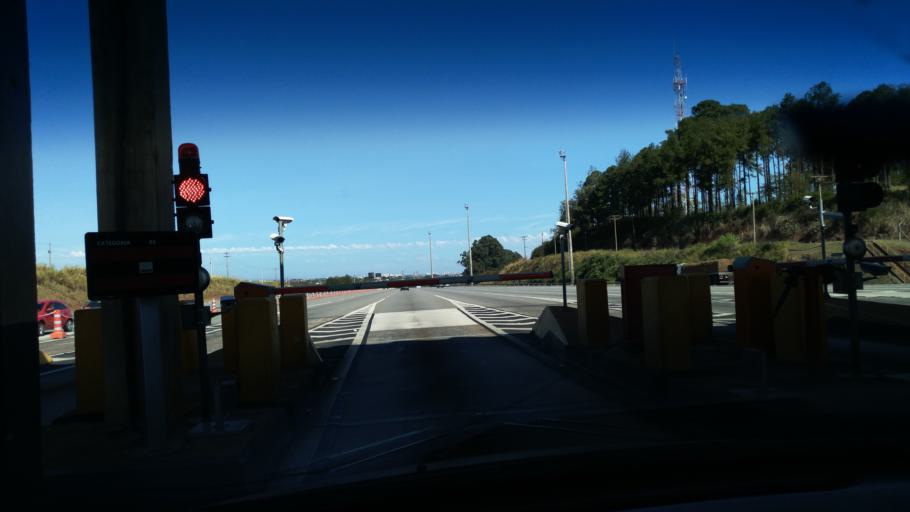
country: BR
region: Sao Paulo
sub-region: Jaguariuna
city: Jaguariuna
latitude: -22.7711
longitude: -47.0221
